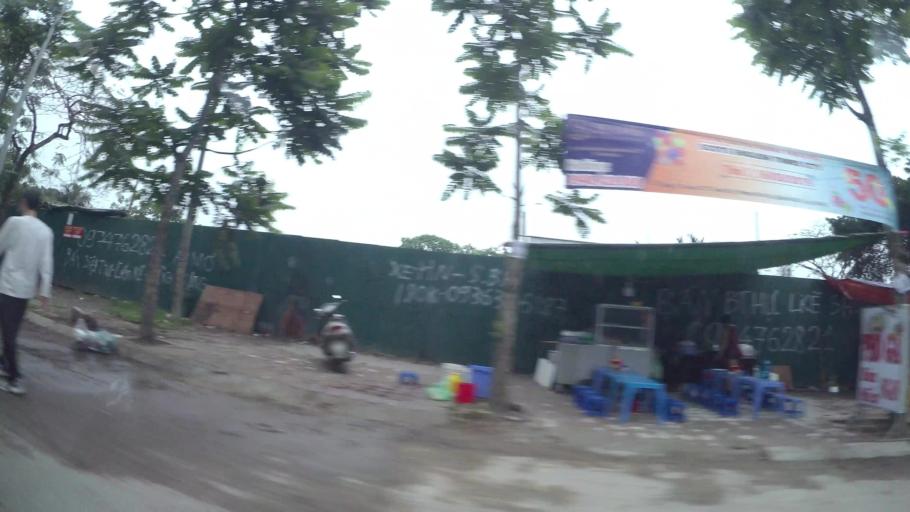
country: VN
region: Ha Noi
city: Hai BaTrung
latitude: 20.9932
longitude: 105.8739
